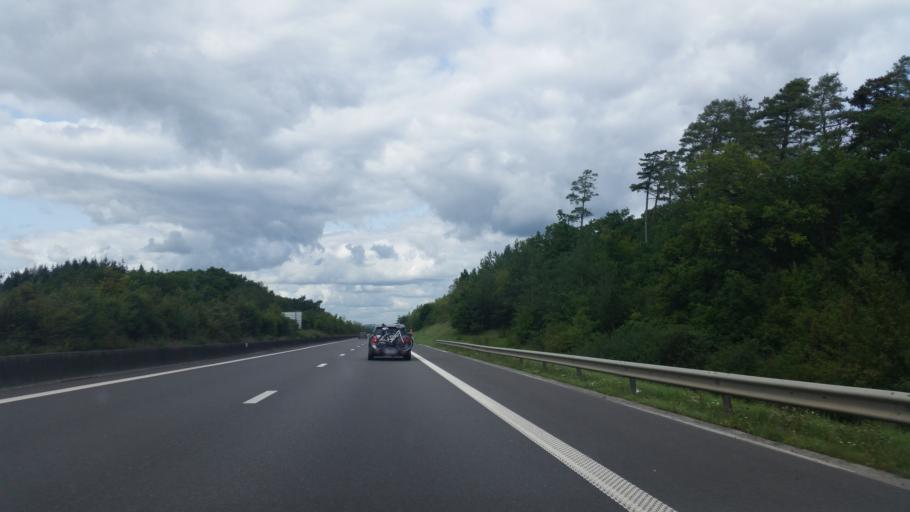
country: BE
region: Wallonia
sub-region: Province du Luxembourg
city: Wellin
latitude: 50.1065
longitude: 5.1165
